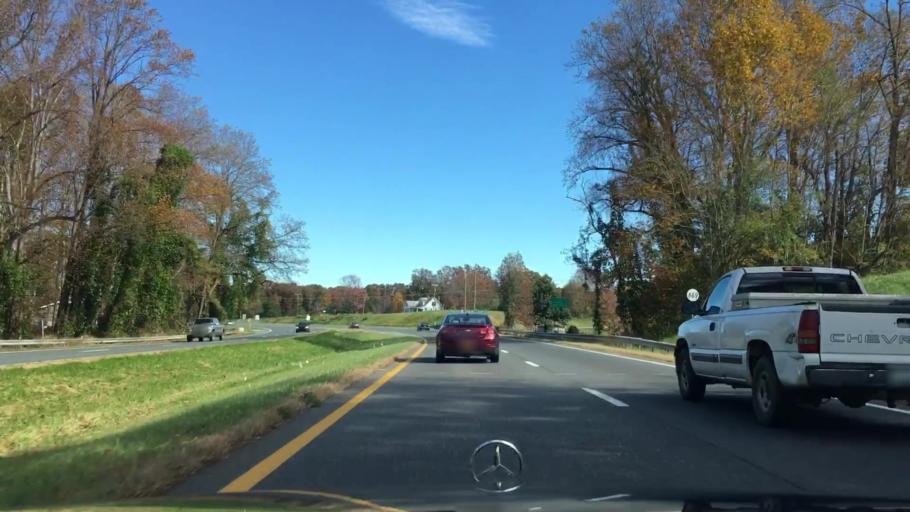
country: US
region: Virginia
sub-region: Campbell County
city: Altavista
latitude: 37.1466
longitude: -79.2320
